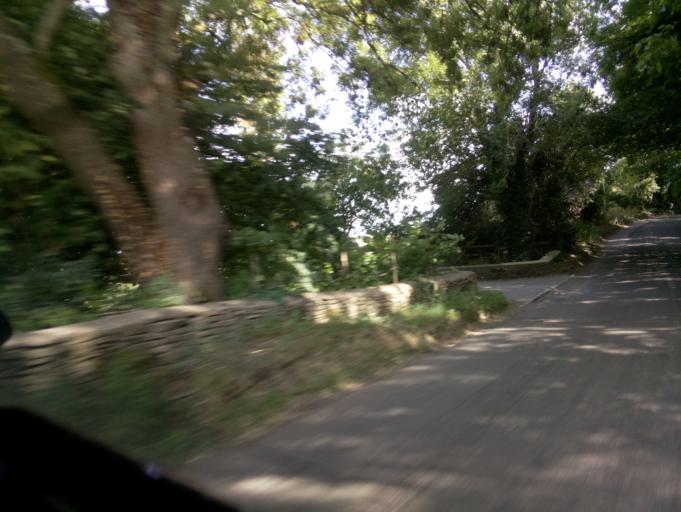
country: GB
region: England
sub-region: Gloucestershire
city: Tetbury
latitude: 51.6589
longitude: -2.1439
